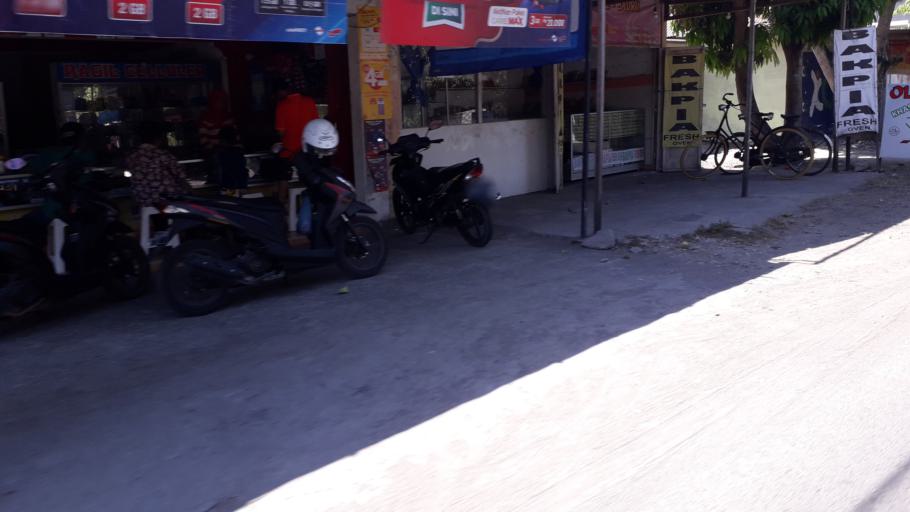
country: ID
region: Daerah Istimewa Yogyakarta
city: Pundong
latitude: -7.9696
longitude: 110.3193
